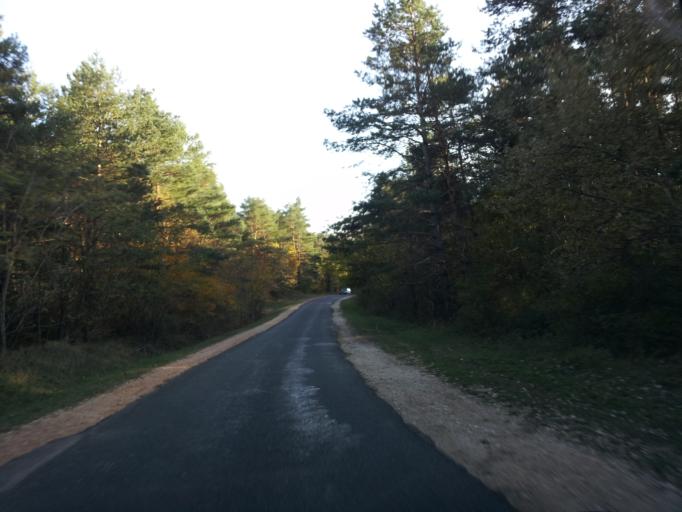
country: HU
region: Gyor-Moson-Sopron
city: Bakonyszentlaszlo
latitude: 47.3731
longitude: 17.8150
